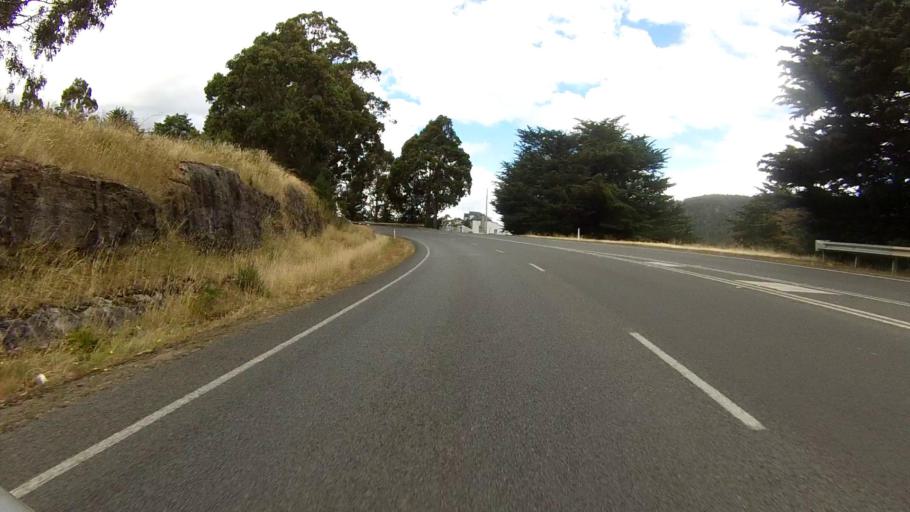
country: AU
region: Tasmania
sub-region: Huon Valley
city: Huonville
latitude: -42.9800
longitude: 147.1309
